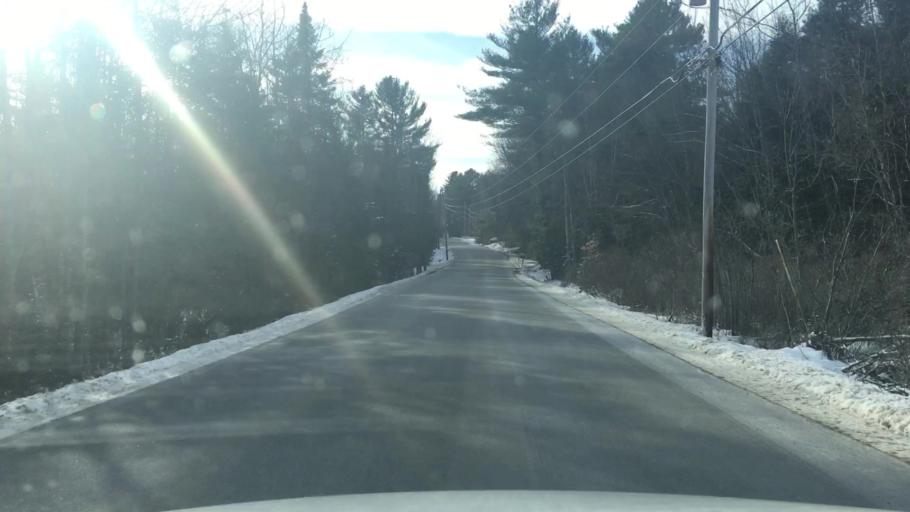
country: US
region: Maine
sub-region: Cumberland County
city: Freeport
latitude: 43.8899
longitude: -70.0859
